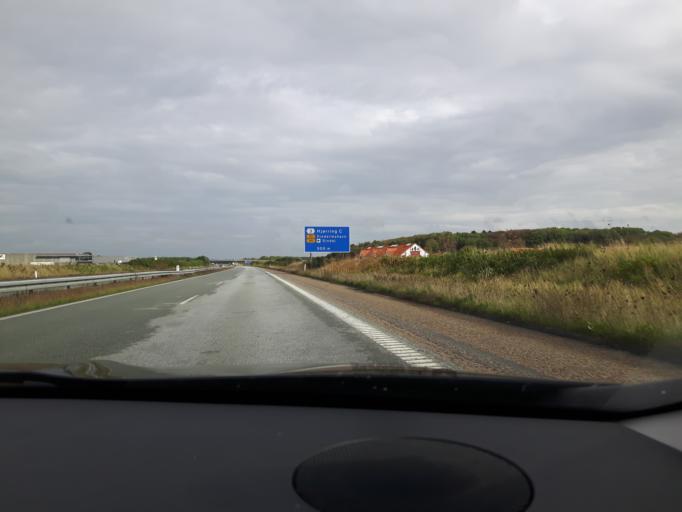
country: DK
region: North Denmark
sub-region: Hjorring Kommune
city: Hjorring
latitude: 57.4490
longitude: 10.0430
